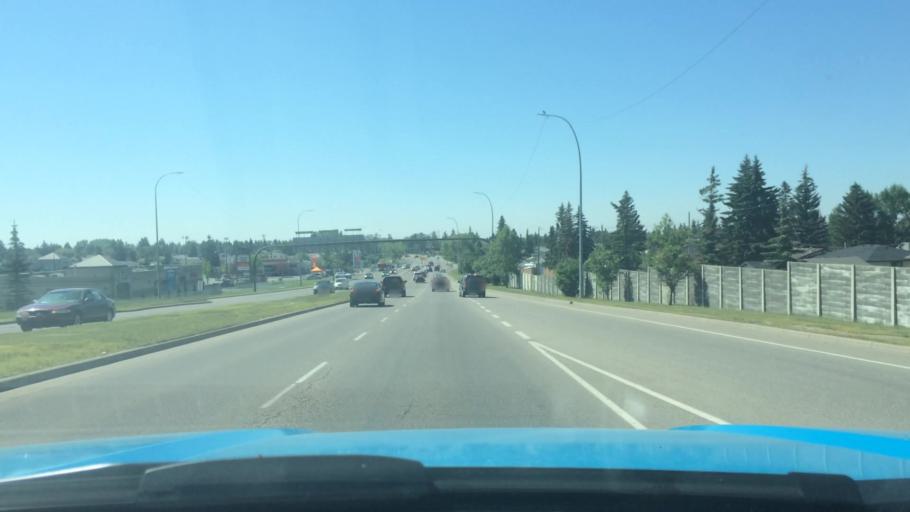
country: CA
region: Alberta
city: Calgary
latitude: 51.0653
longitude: -113.9585
